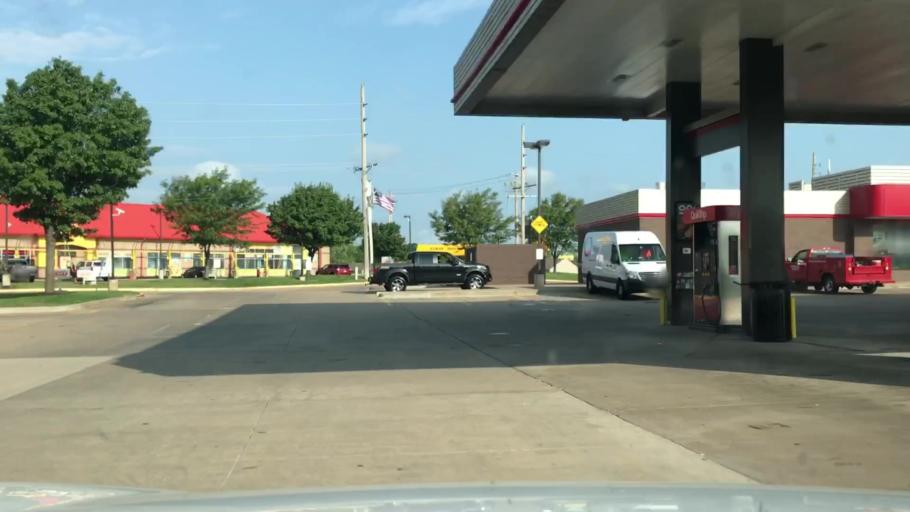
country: US
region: Missouri
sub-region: Saint Charles County
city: Dardenne Prairie
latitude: 38.7997
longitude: -90.7354
